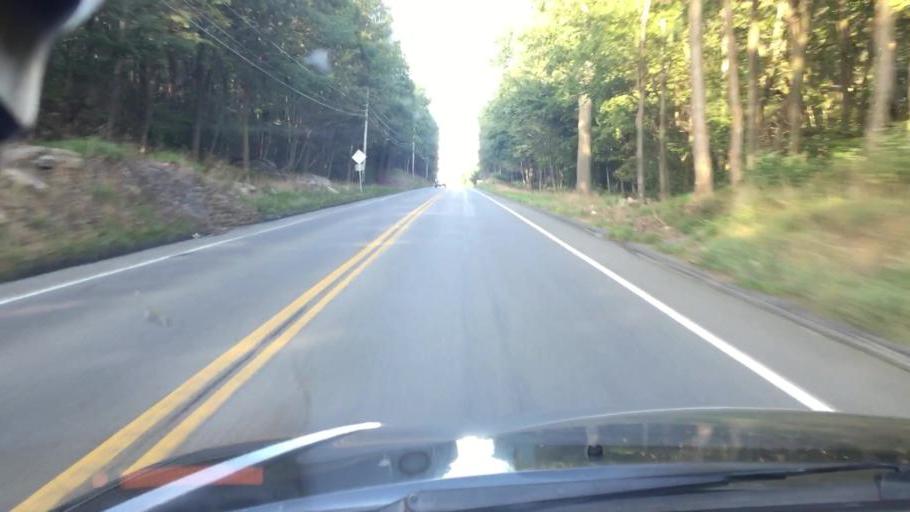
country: US
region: Pennsylvania
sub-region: Carbon County
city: Jim Thorpe
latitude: 40.8908
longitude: -75.6965
